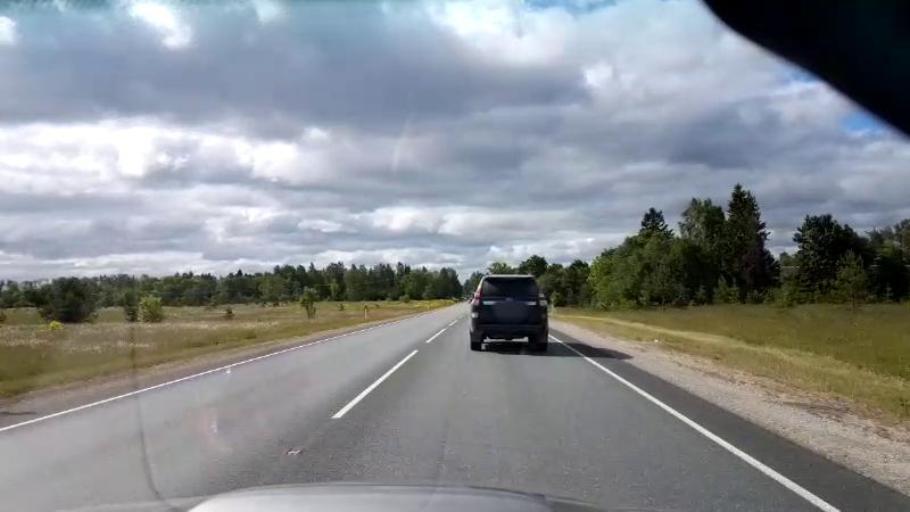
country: EE
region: Raplamaa
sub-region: Maerjamaa vald
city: Marjamaa
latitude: 58.9707
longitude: 24.4759
